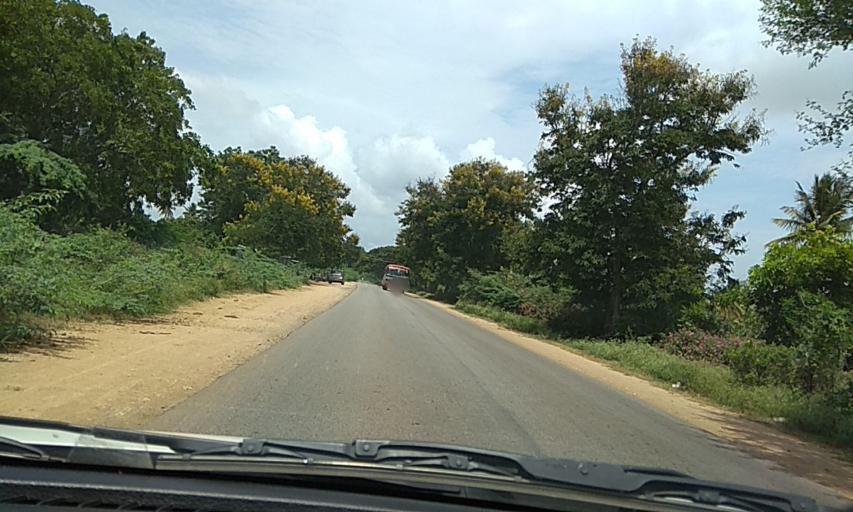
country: IN
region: Karnataka
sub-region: Chamrajnagar
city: Gundlupet
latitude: 11.8110
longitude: 76.7298
